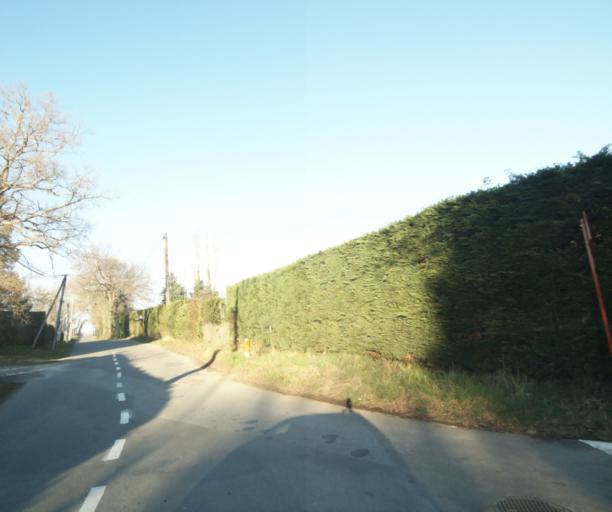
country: FR
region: Aquitaine
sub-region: Departement des Pyrenees-Atlantiques
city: Urrugne
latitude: 43.3427
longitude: -1.6994
